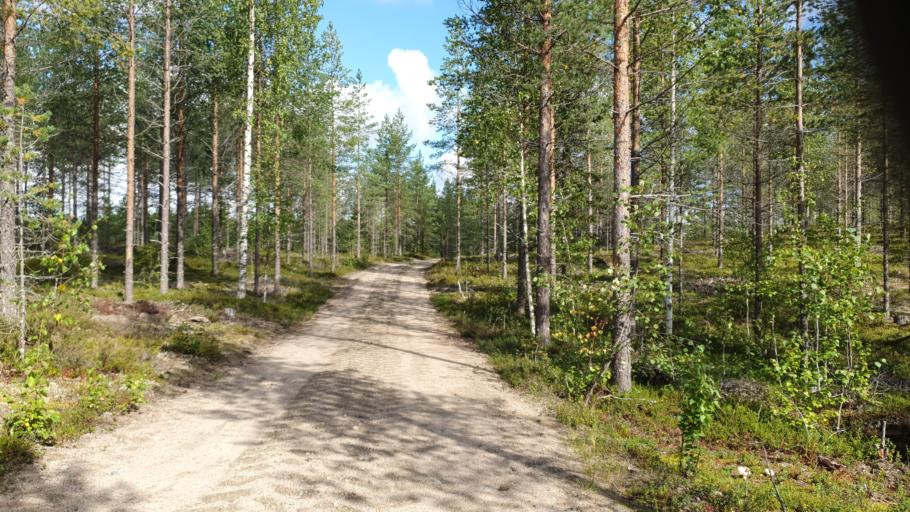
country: FI
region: Kainuu
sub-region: Kehys-Kainuu
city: Kuhmo
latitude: 64.1483
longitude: 29.3565
